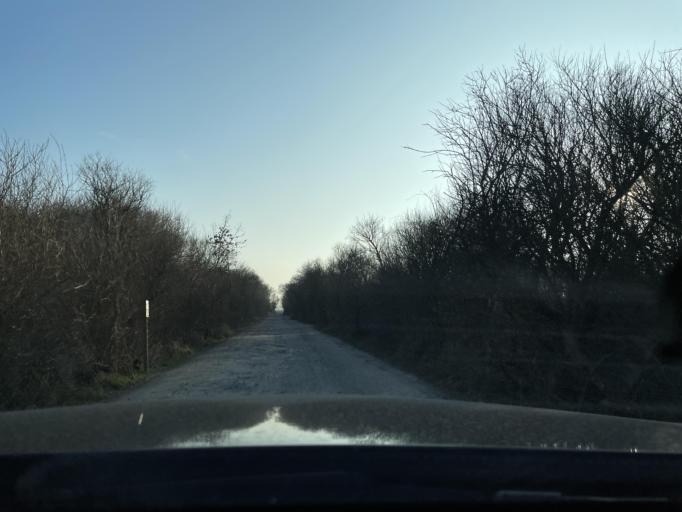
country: GB
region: England
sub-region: Norfolk
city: Martham
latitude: 52.7577
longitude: 1.6487
